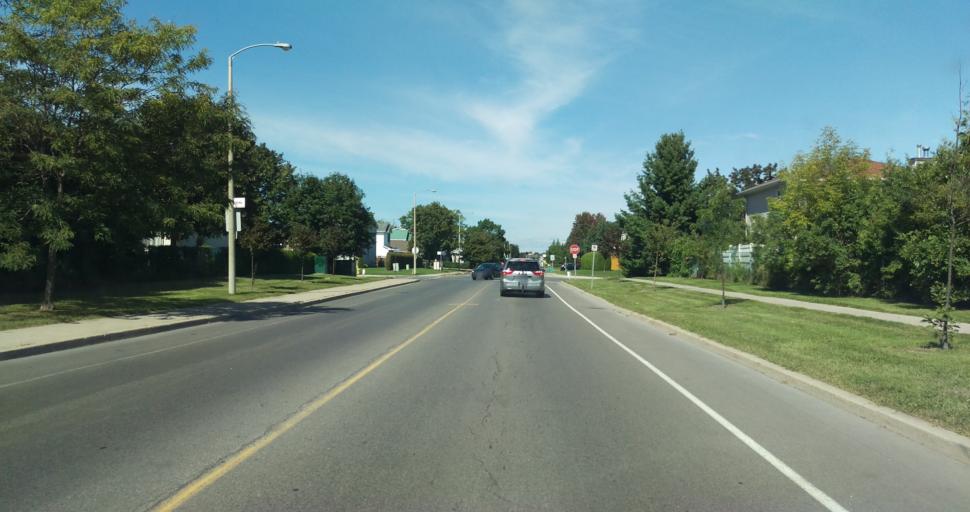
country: CA
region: Ontario
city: Clarence-Rockland
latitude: 45.4659
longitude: -75.4773
